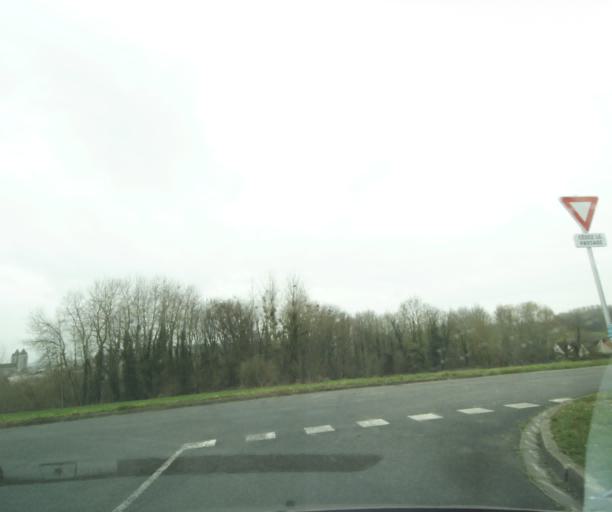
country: FR
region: Picardie
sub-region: Departement de l'Oise
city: Noyon
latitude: 49.5865
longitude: 3.0132
